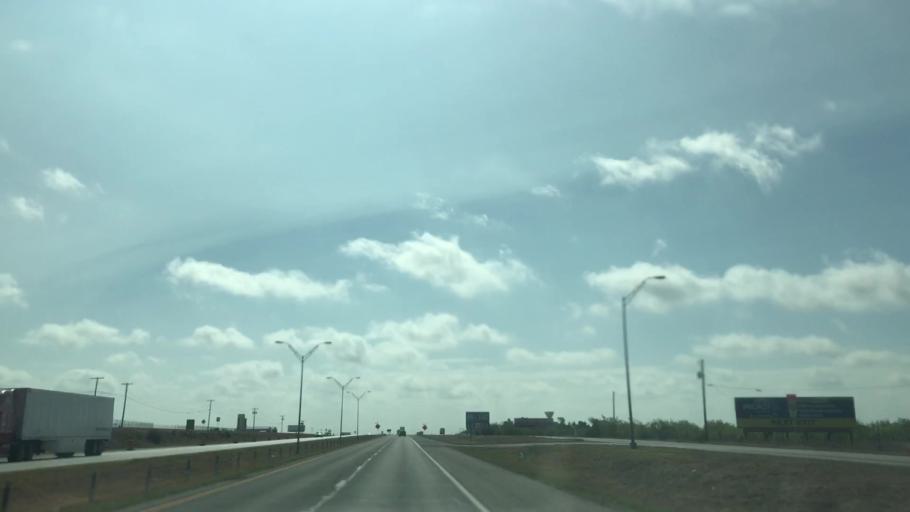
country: US
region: Texas
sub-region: Nolan County
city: Sweetwater
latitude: 32.4532
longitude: -100.4618
